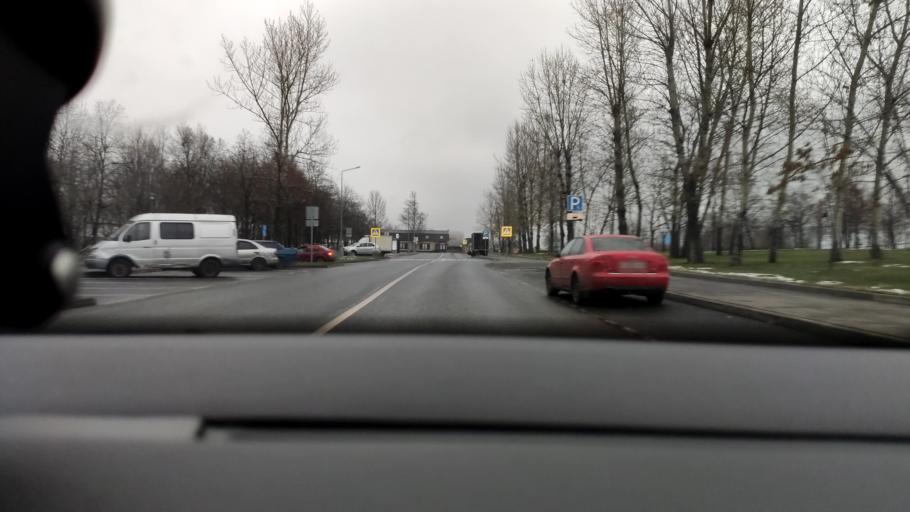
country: RU
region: Moskovskaya
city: Alekseyevka
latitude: 55.6316
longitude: 37.8023
